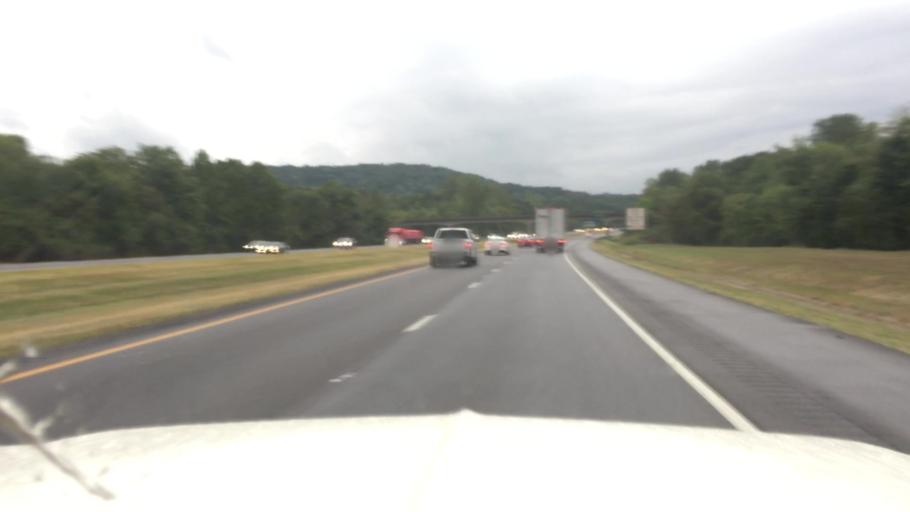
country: US
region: Alabama
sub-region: Morgan County
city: Falkville
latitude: 34.3413
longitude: -86.8933
